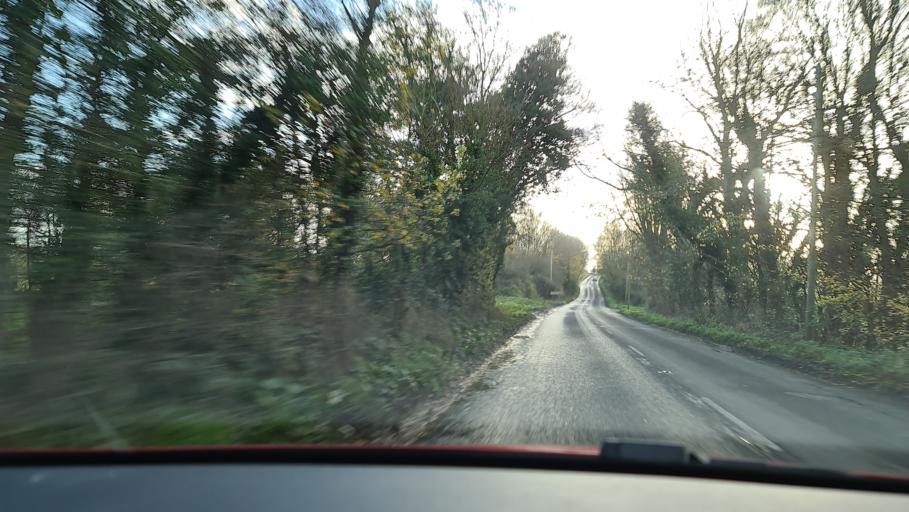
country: GB
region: England
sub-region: Buckinghamshire
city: Haddenham
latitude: 51.7955
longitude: -0.9433
